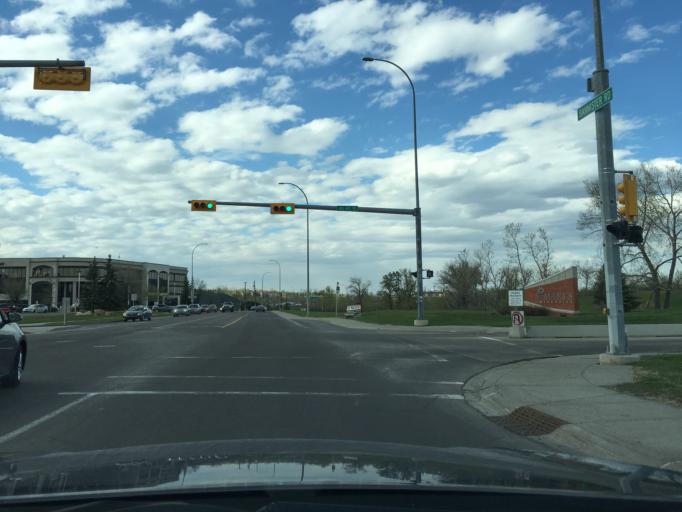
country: CA
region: Alberta
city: Calgary
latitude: 50.9225
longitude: -114.0698
